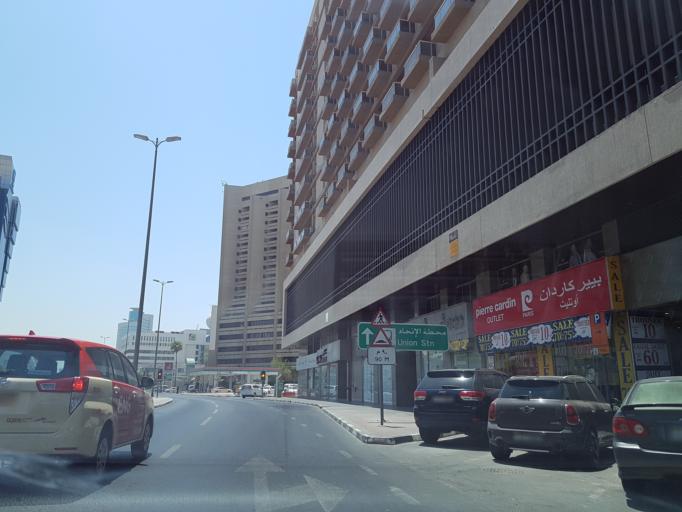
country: AE
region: Ash Shariqah
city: Sharjah
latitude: 25.2668
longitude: 55.3092
